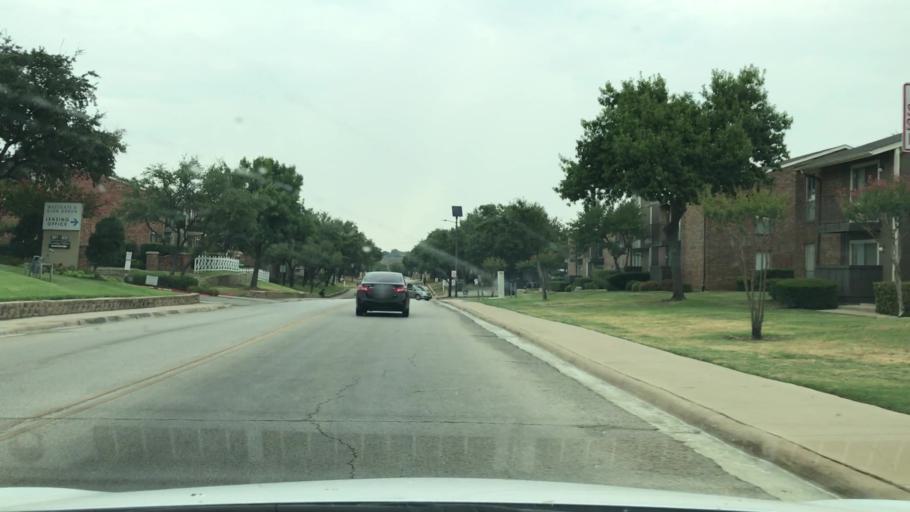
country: US
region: Texas
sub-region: Dallas County
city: Irving
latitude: 32.8621
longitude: -96.9964
